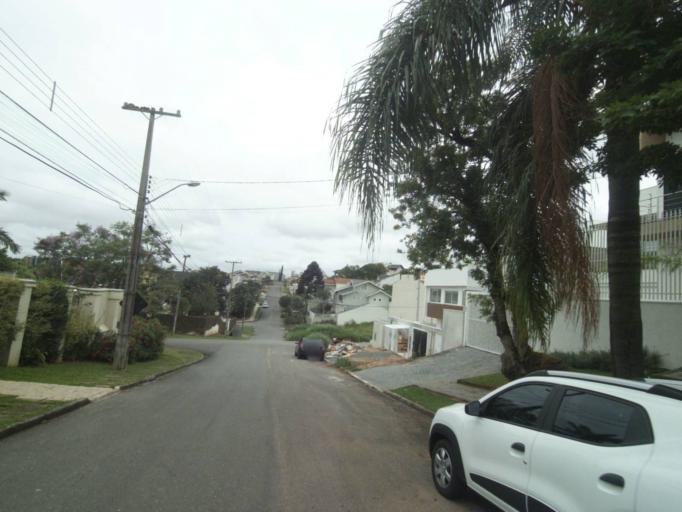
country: BR
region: Parana
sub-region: Curitiba
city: Curitiba
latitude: -25.4426
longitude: -49.3324
